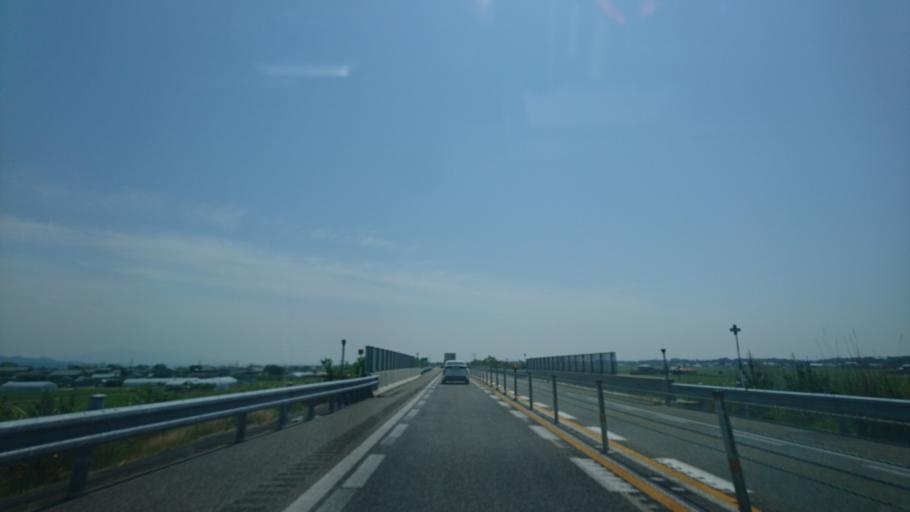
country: JP
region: Niigata
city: Shibata
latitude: 38.0809
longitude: 139.3878
